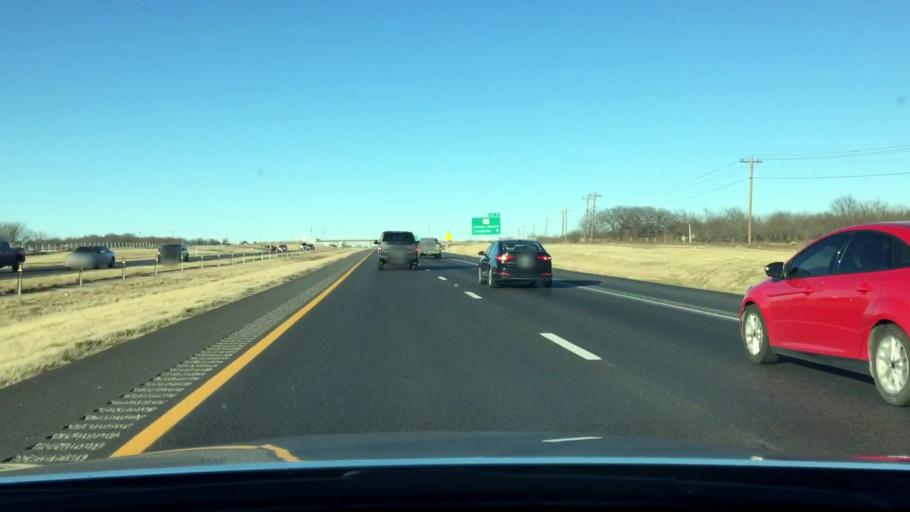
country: US
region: Texas
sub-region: Denton County
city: Roanoke
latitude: 33.0573
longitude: -97.2461
